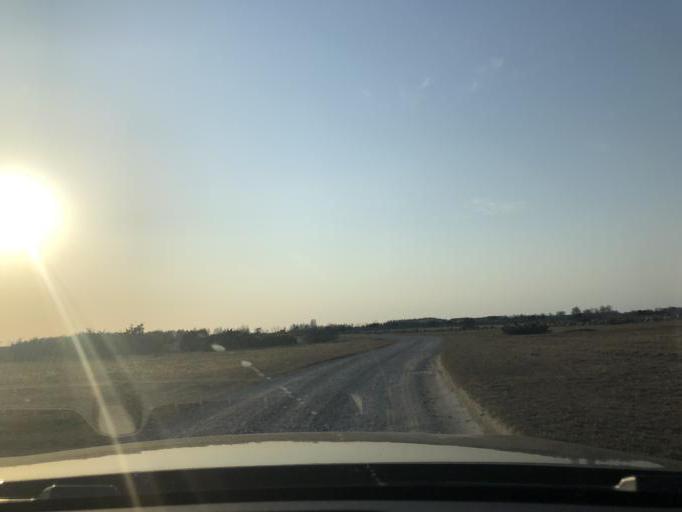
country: SE
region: Kalmar
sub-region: Morbylanga Kommun
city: Sodra Sandby
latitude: 56.5578
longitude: 16.6335
